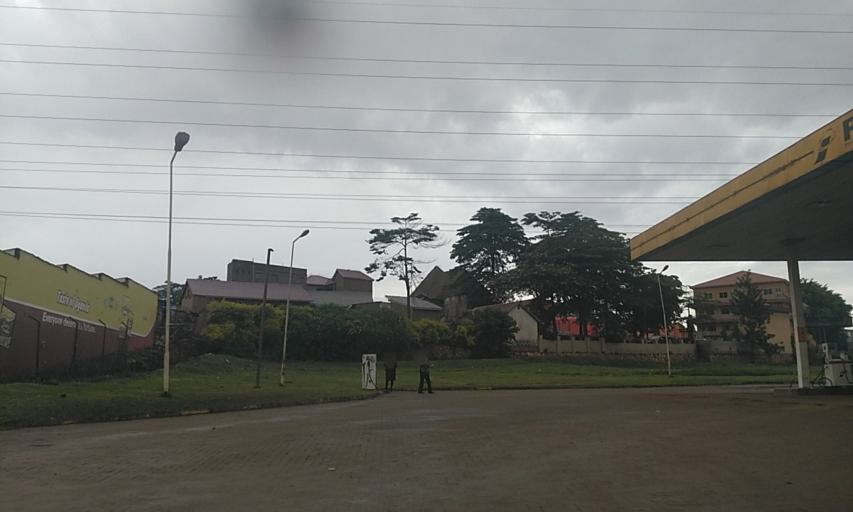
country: UG
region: Central Region
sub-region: Wakiso District
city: Kireka
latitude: 0.3429
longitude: 32.6374
